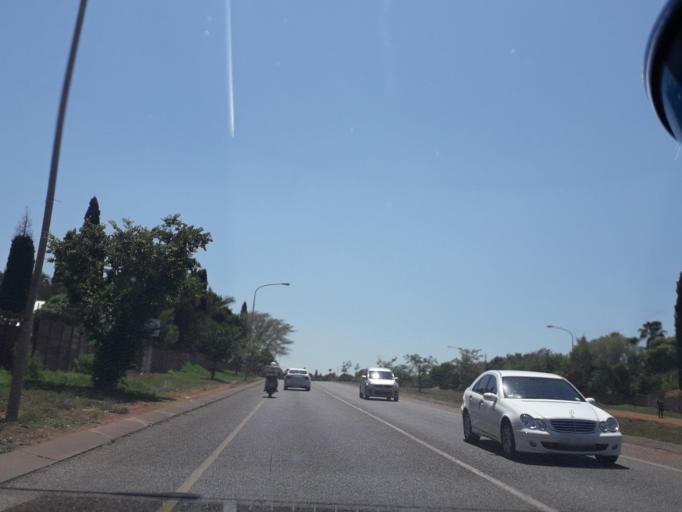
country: ZA
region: Gauteng
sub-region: City of Tshwane Metropolitan Municipality
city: Centurion
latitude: -25.8702
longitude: 28.1775
